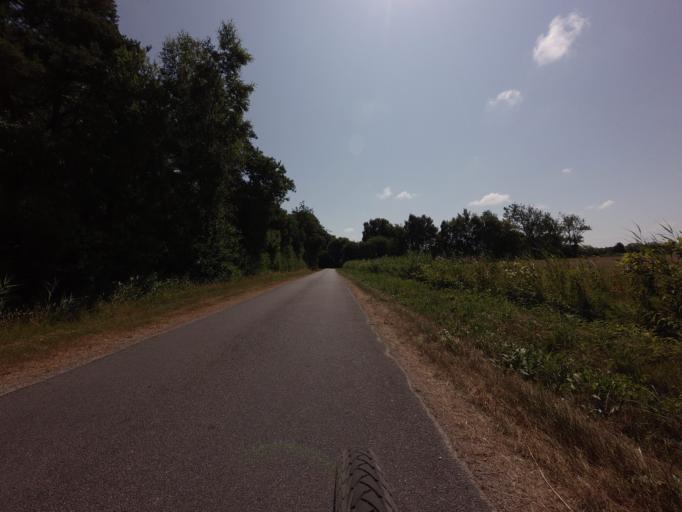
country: DK
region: North Denmark
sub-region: Laeso Kommune
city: Byrum
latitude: 57.2533
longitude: 10.9793
